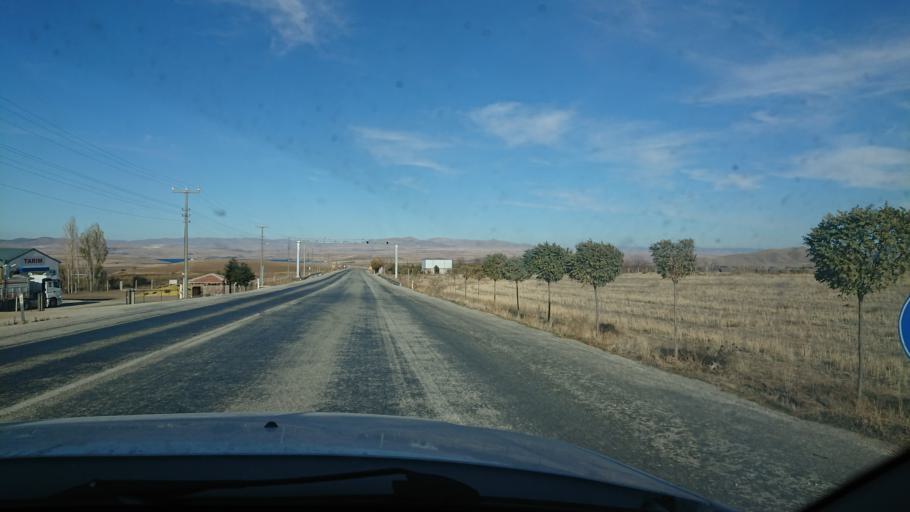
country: TR
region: Aksaray
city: Sariyahsi
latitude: 38.9932
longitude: 33.8485
